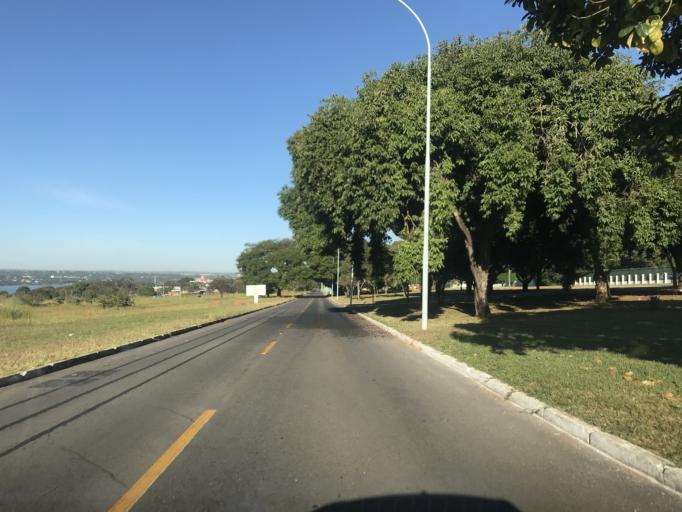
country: BR
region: Federal District
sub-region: Brasilia
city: Brasilia
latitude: -15.8162
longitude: -47.8826
